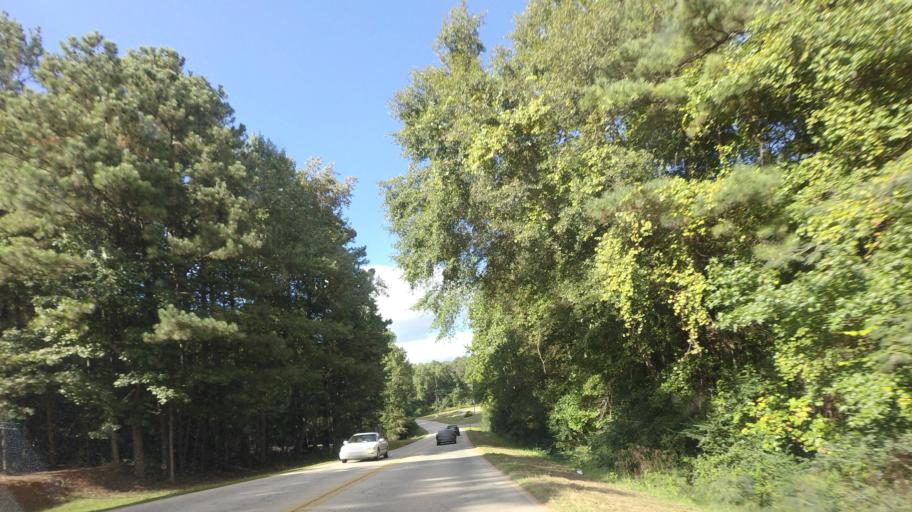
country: US
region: Georgia
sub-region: Lamar County
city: Barnesville
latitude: 33.0677
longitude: -84.1560
